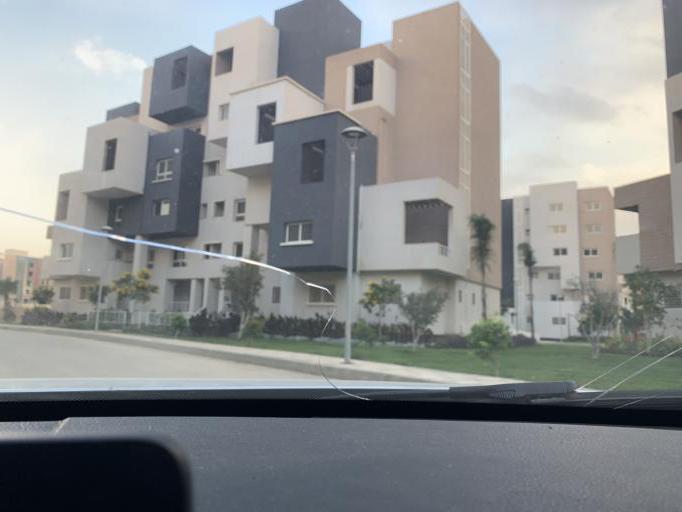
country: EG
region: Muhafazat al Qalyubiyah
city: Al Khankah
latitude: 30.0996
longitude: 31.6529
